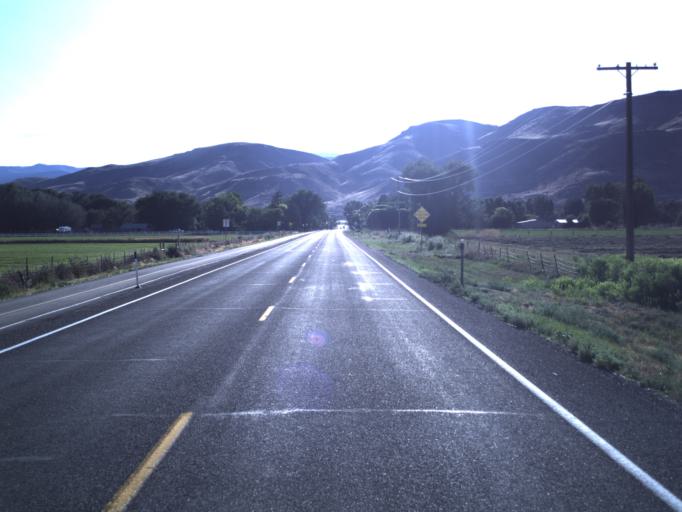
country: US
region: Utah
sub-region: Sevier County
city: Monroe
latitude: 38.6832
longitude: -112.1361
